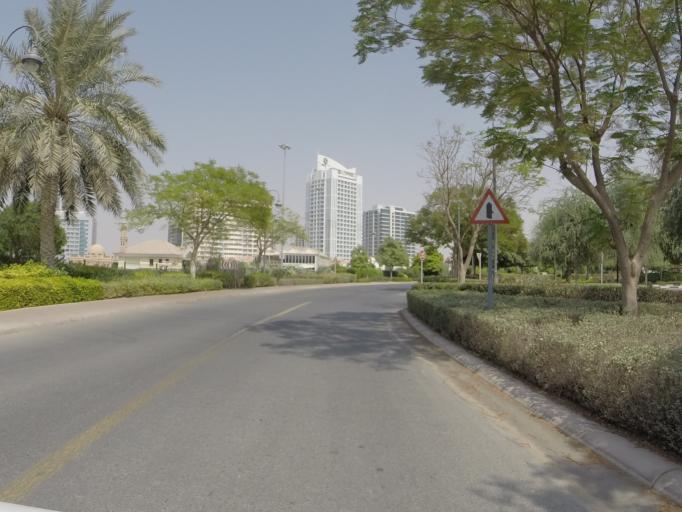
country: AE
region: Dubai
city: Dubai
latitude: 25.0316
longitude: 55.2192
